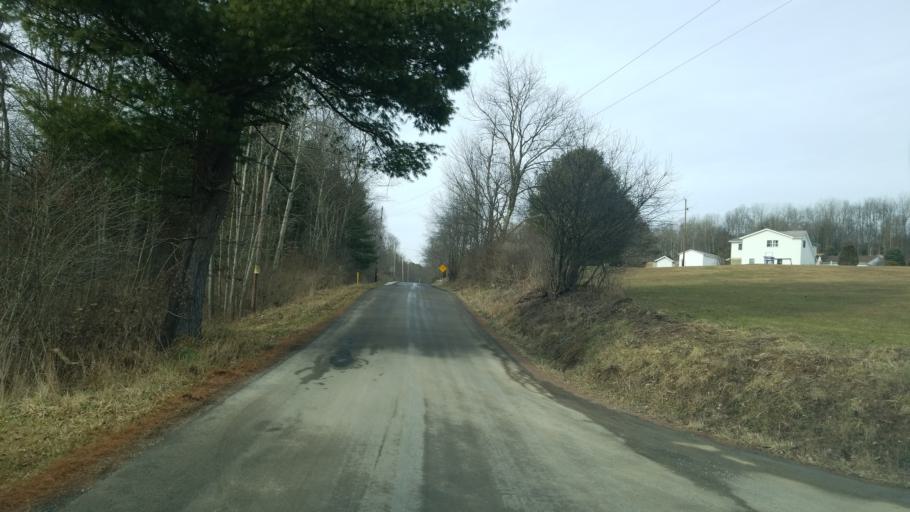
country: US
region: Pennsylvania
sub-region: Jefferson County
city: Punxsutawney
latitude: 40.8420
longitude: -78.9959
